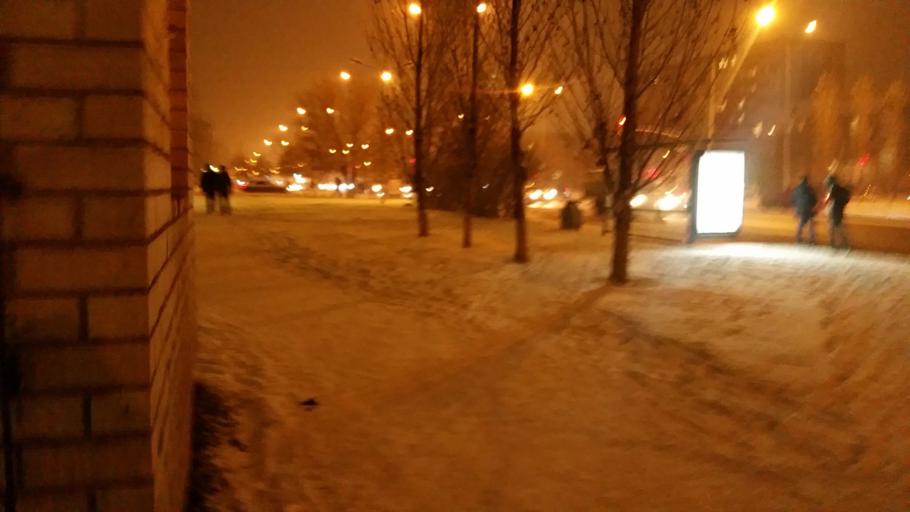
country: KZ
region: Astana Qalasy
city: Astana
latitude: 51.1525
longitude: 71.4808
